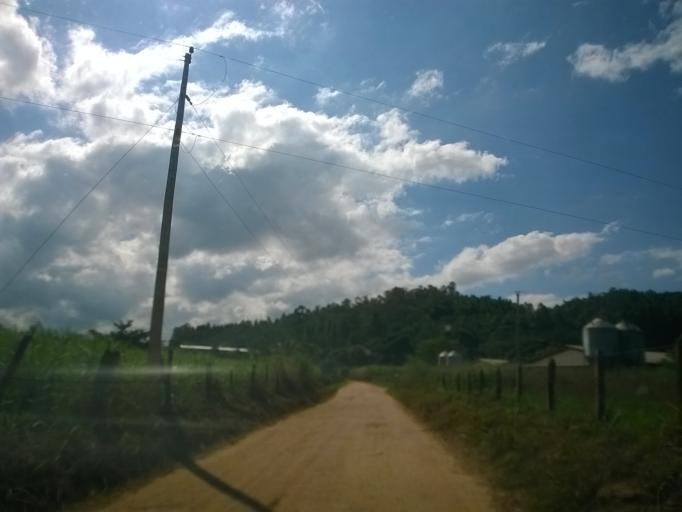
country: BR
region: Minas Gerais
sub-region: Uba
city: Uba
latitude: -21.0570
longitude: -42.9010
